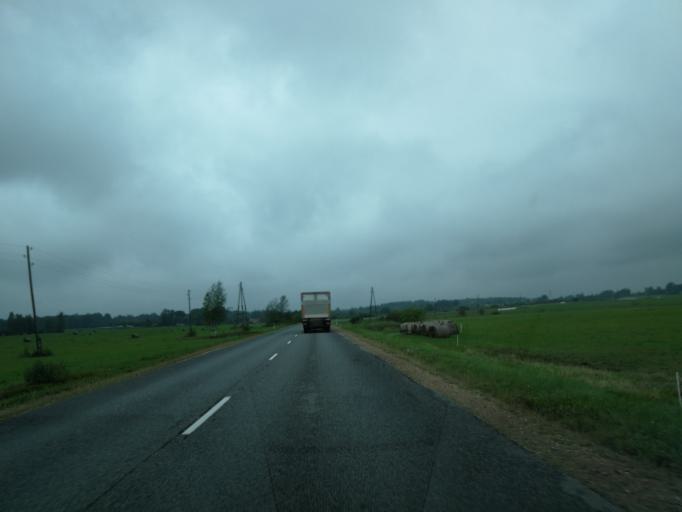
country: LV
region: Livani
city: Livani
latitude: 56.3548
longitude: 26.2366
